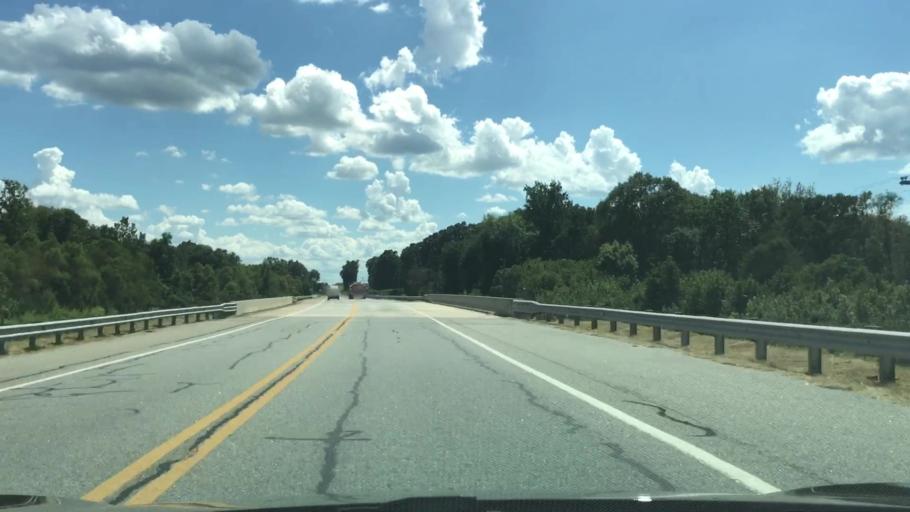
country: US
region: Georgia
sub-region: Oconee County
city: Watkinsville
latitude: 33.7371
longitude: -83.3036
